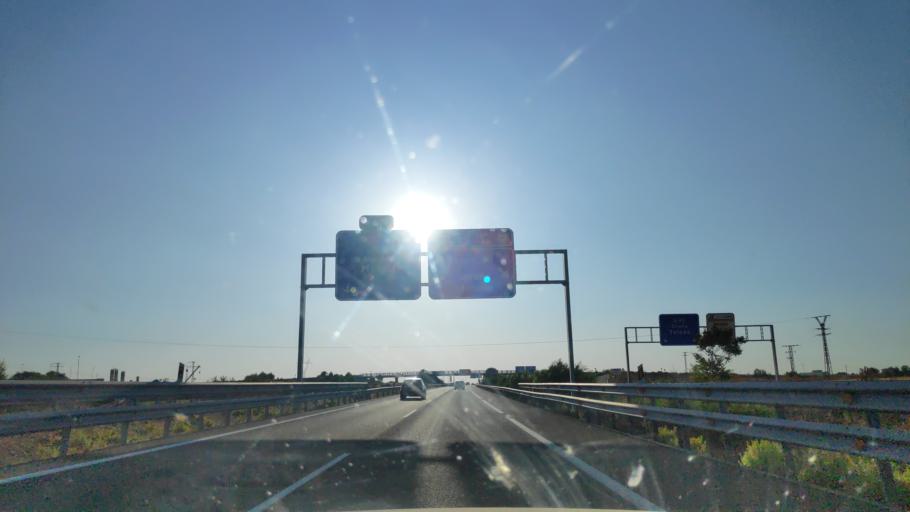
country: ES
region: Castille-La Mancha
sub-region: Provincia de Cuenca
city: Tarancon
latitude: 39.9941
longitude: -3.0046
